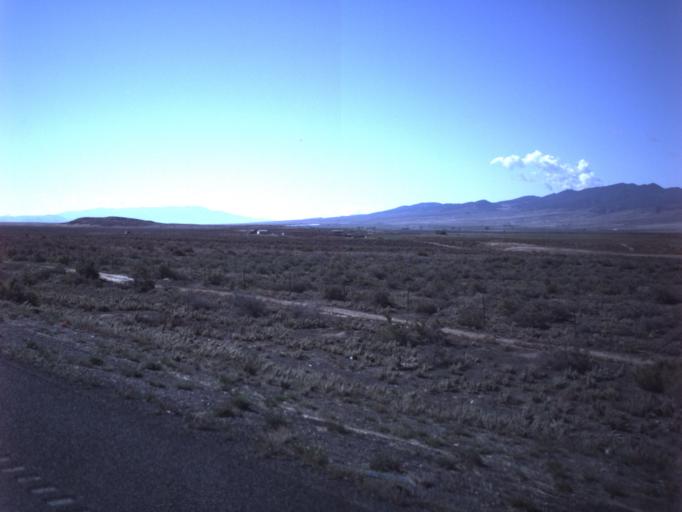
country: US
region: Utah
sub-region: Sanpete County
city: Gunnison
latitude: 39.2020
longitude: -111.8467
